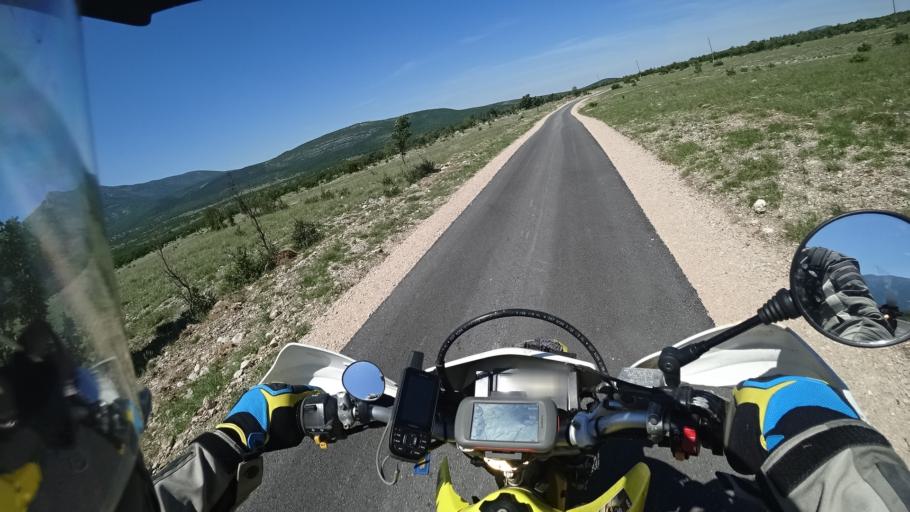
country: BA
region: Federation of Bosnia and Herzegovina
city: Bosansko Grahovo
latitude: 44.0057
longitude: 16.3770
